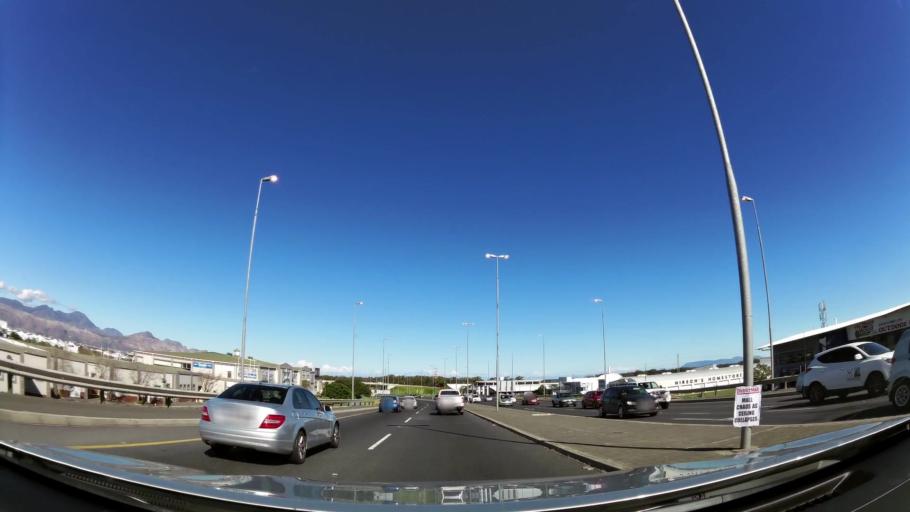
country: ZA
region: Western Cape
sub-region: Cape Winelands District Municipality
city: Stellenbosch
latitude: -34.0786
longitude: 18.8201
